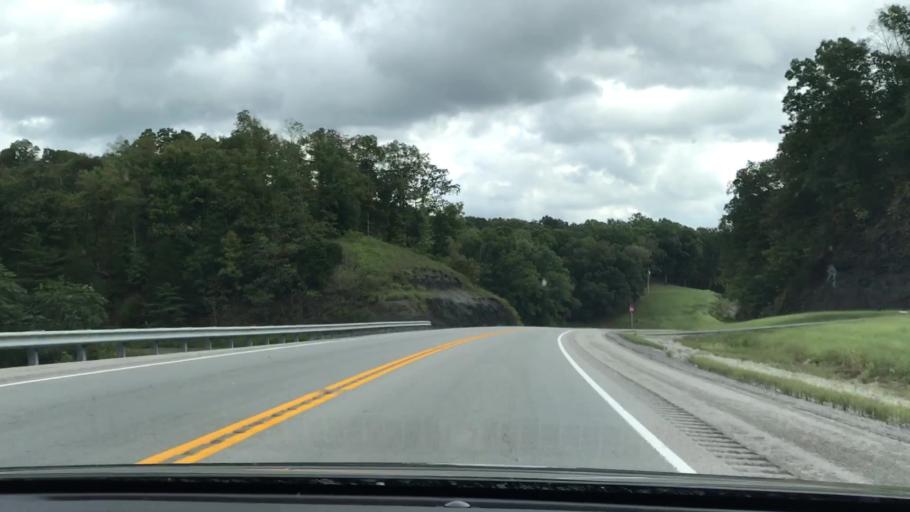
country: US
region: Kentucky
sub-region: Cumberland County
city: Burkesville
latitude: 36.8002
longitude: -85.3818
